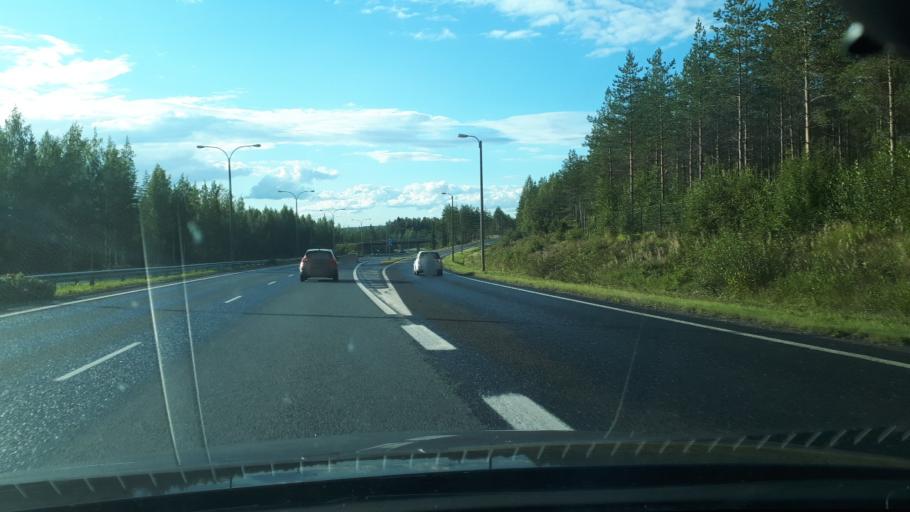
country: FI
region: Northern Savo
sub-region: Kuopio
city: Siilinjaervi
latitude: 63.0154
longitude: 27.6691
